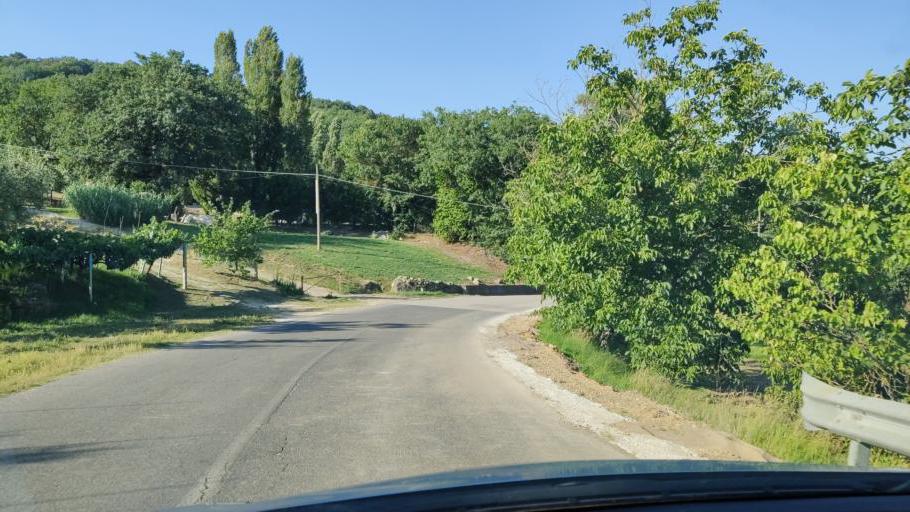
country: IT
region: Umbria
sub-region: Provincia di Terni
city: Penna in Teverina
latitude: 42.4894
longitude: 12.3680
